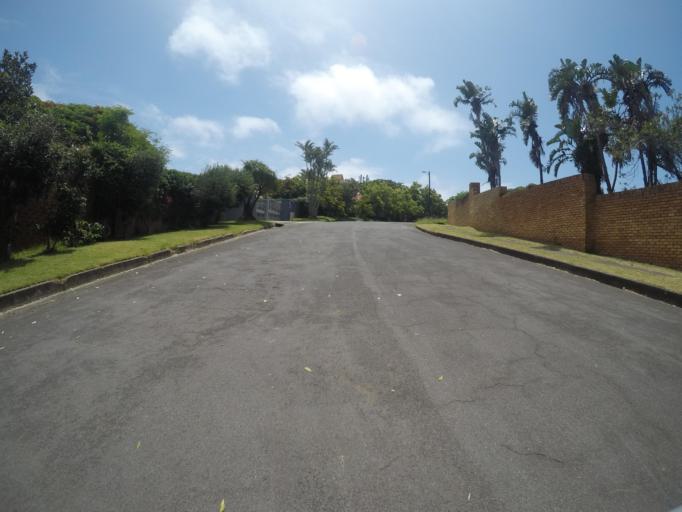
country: ZA
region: Eastern Cape
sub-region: Buffalo City Metropolitan Municipality
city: East London
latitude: -32.9992
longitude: 27.9285
